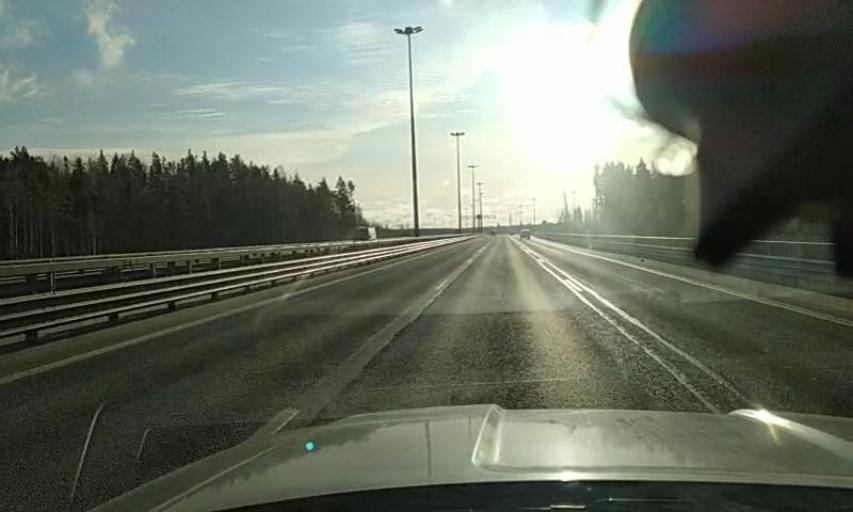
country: RU
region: St.-Petersburg
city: Pesochnyy
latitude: 60.0921
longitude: 30.0972
